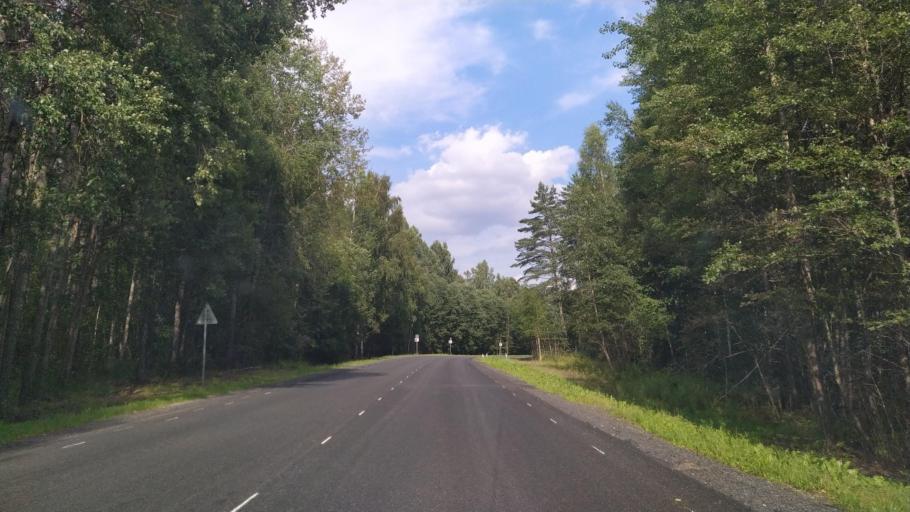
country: RU
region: Pskov
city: Porkhov
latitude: 57.7391
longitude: 29.4189
